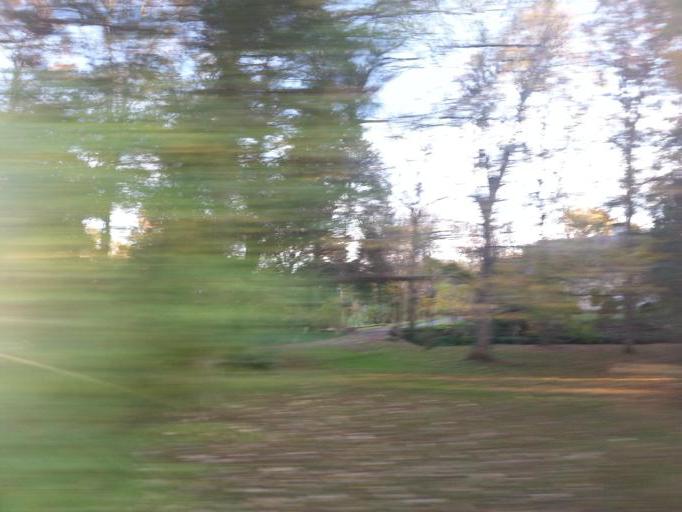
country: US
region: Tennessee
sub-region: Knox County
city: Knoxville
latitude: 35.9222
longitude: -83.9980
